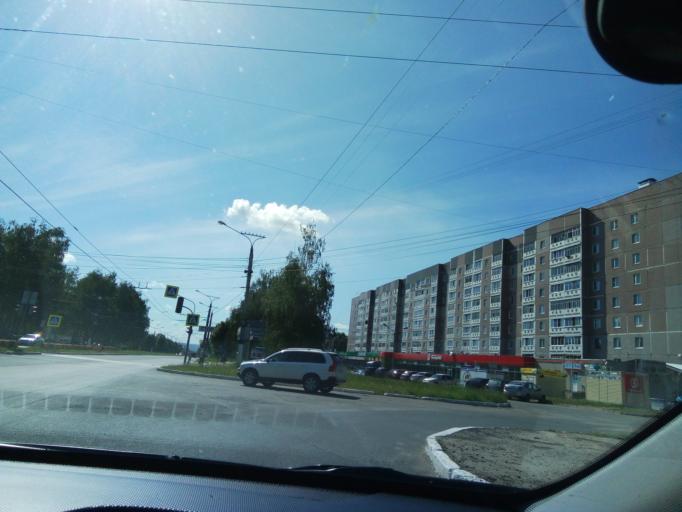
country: RU
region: Chuvashia
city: Novocheboksarsk
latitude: 56.1172
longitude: 47.4807
